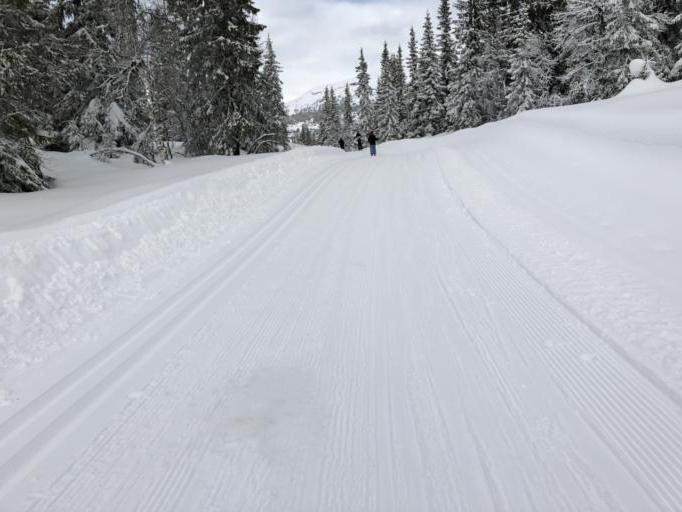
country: NO
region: Oppland
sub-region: Gausdal
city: Segalstad bru
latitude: 61.3241
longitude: 10.0781
